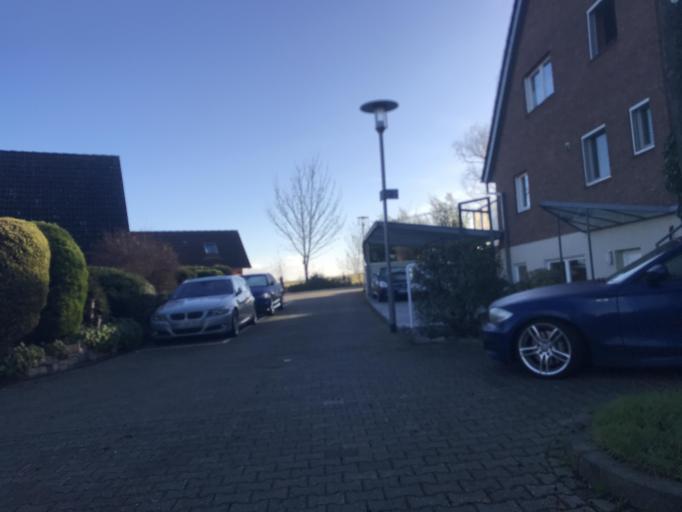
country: DE
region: Rheinland-Pfalz
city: Mainz
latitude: 49.9677
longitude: 8.2892
